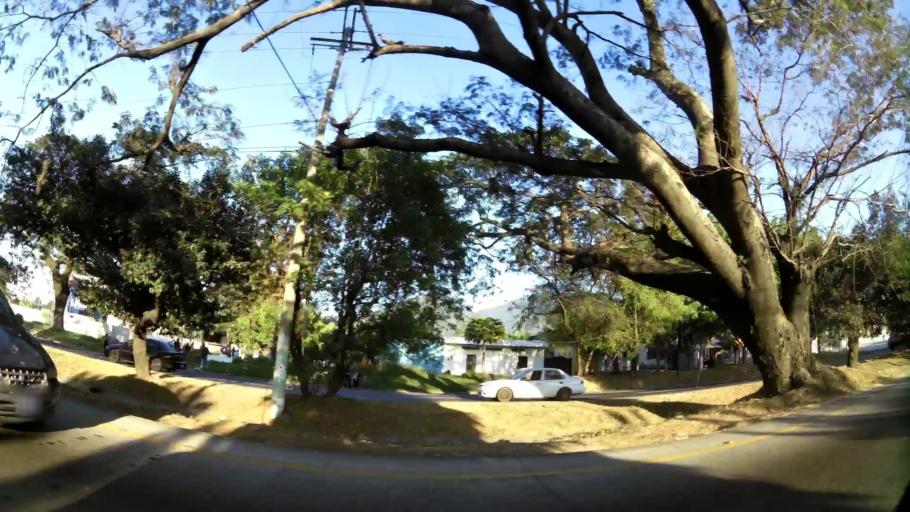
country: SV
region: La Libertad
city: Santa Tecla
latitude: 13.7418
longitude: -89.3628
